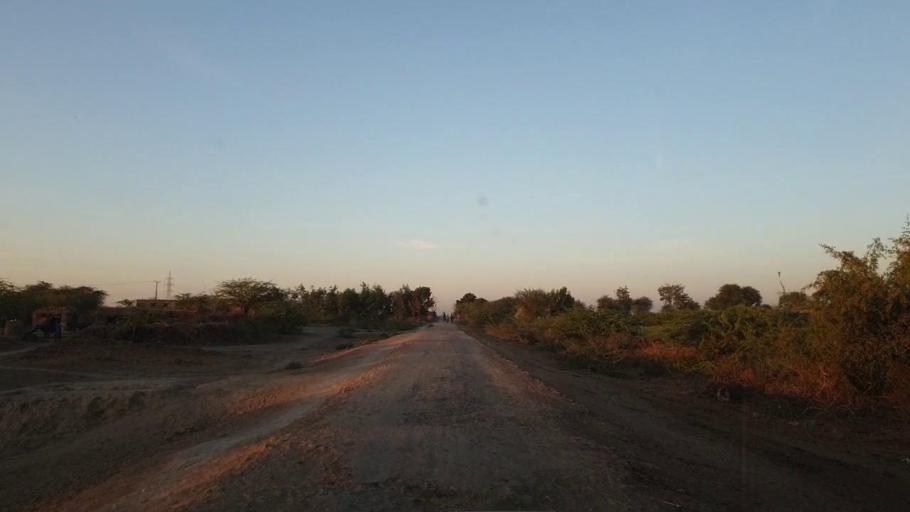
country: PK
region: Sindh
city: Kunri
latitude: 25.1448
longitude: 69.4454
